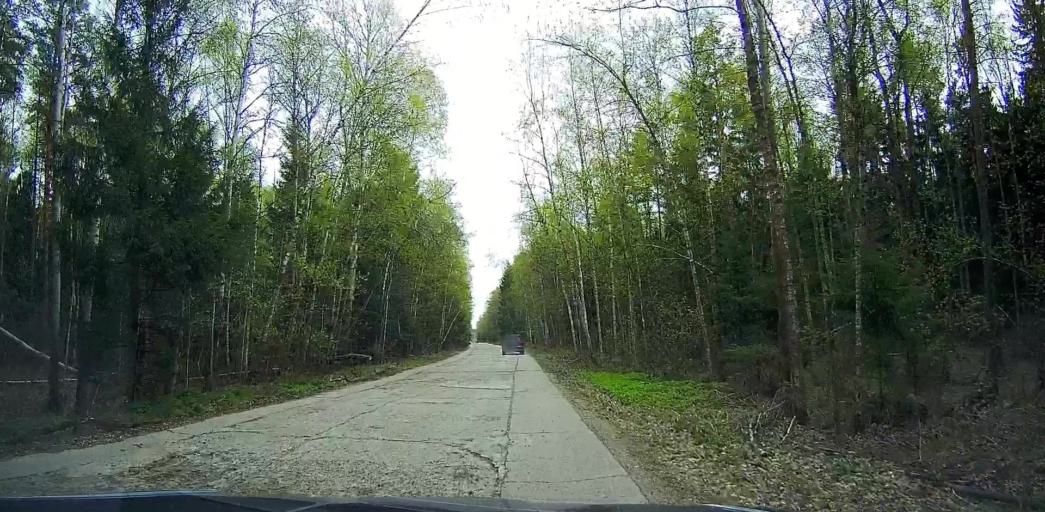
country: RU
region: Moskovskaya
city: Malyshevo
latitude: 55.5356
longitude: 38.3882
